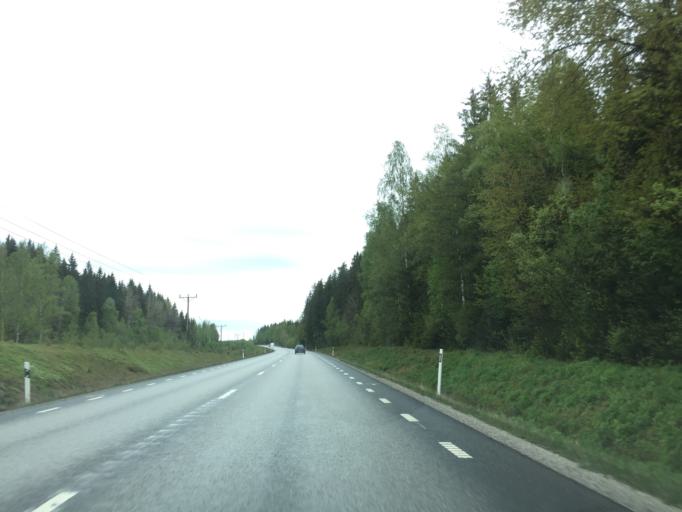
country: SE
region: OErebro
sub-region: Lindesbergs Kommun
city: Lindesberg
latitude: 59.5752
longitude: 15.2053
